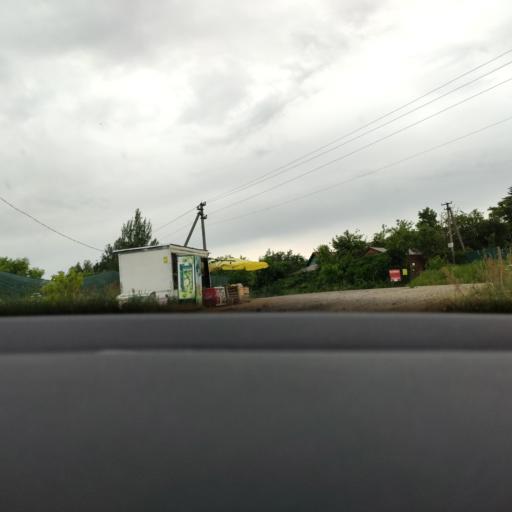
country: RU
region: Moskovskaya
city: Dedenevo
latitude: 56.2569
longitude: 37.5665
